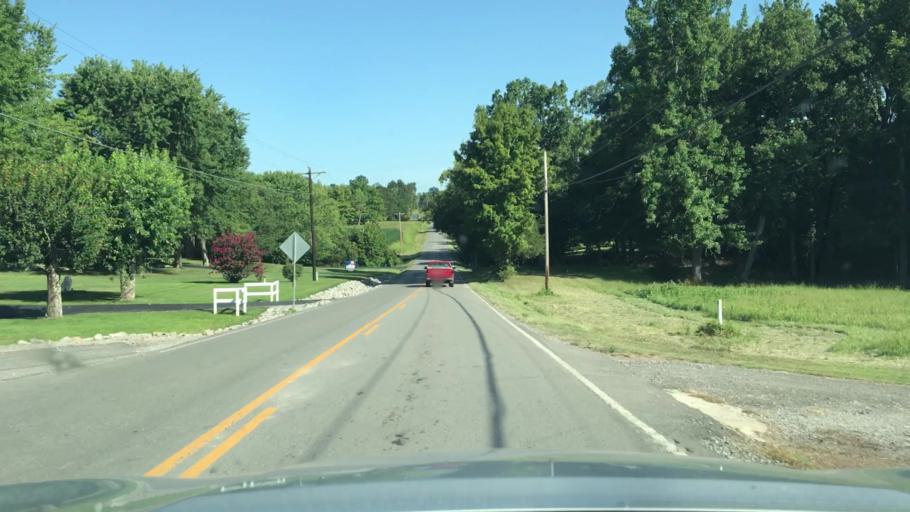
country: US
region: Kentucky
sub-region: Muhlenberg County
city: Greenville
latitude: 37.1674
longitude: -87.1475
